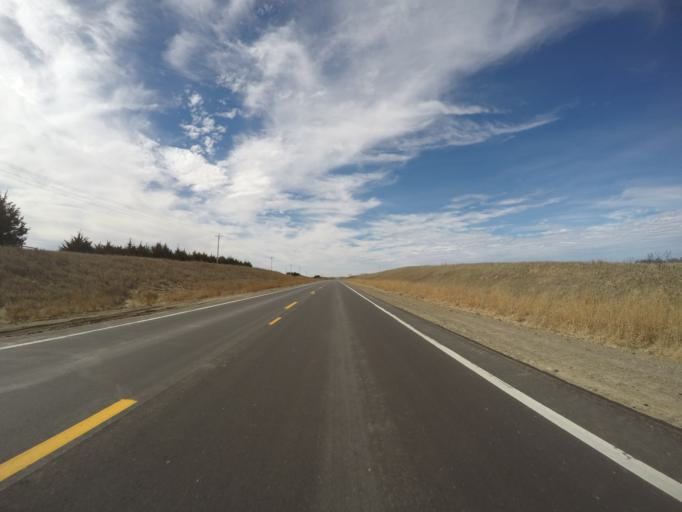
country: US
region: Nebraska
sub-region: Franklin County
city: Franklin
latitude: 40.0962
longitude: -98.8867
